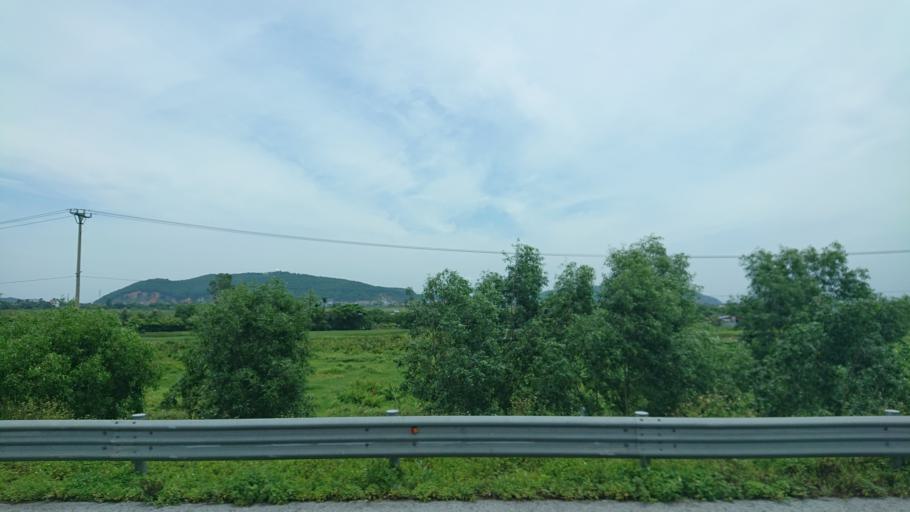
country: VN
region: Hai Phong
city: Nui Doi
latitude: 20.7706
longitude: 106.6197
